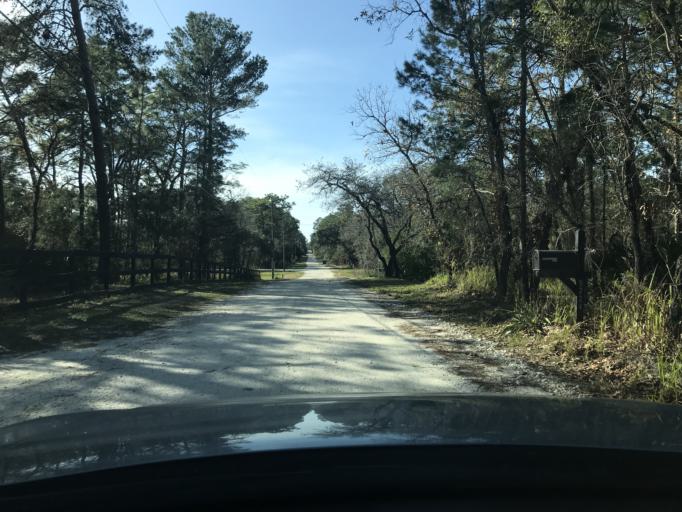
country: US
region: Florida
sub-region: Hernando County
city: North Weeki Wachee
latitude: 28.5517
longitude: -82.5691
